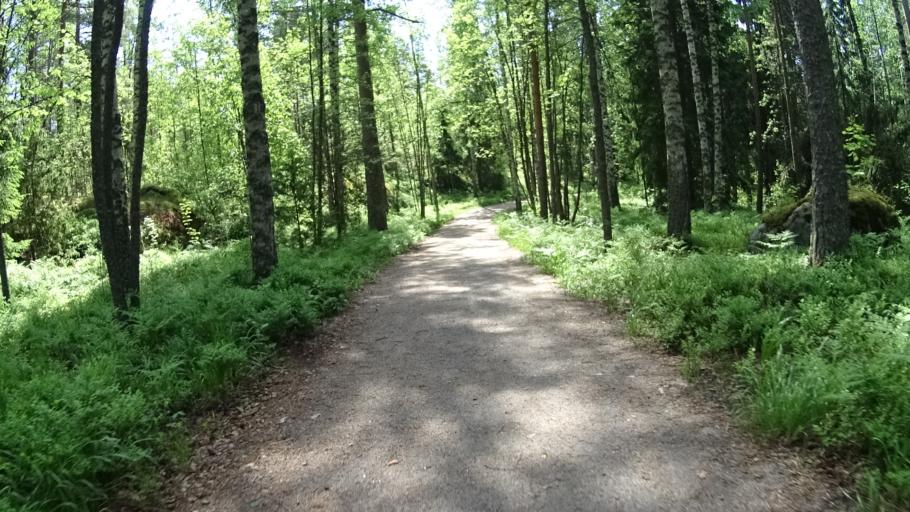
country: FI
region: Uusimaa
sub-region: Helsinki
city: Kauniainen
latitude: 60.3165
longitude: 24.6809
